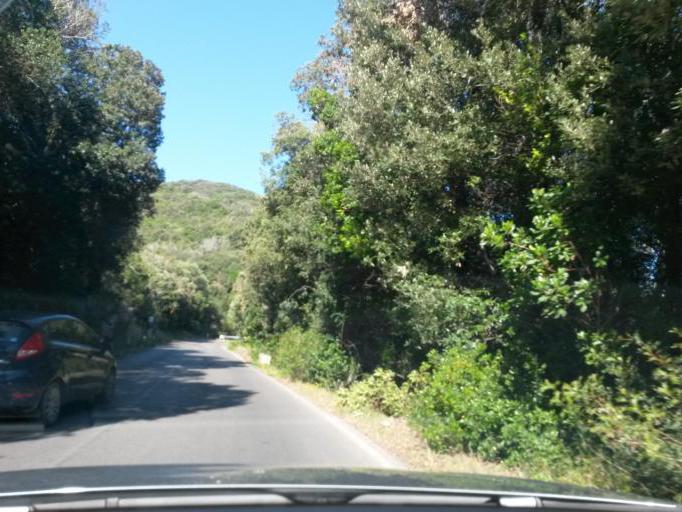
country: IT
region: Tuscany
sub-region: Provincia di Livorno
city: Campo nell'Elba
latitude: 42.7849
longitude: 10.2373
